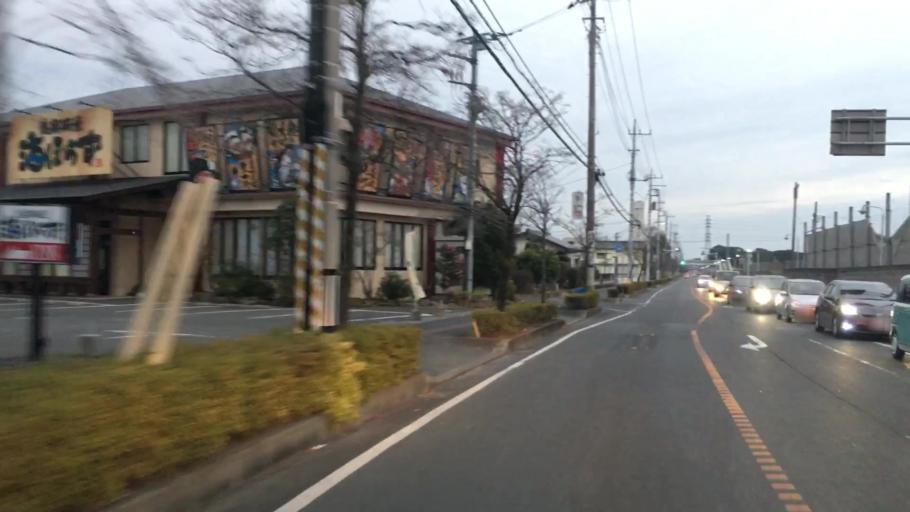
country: JP
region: Gunma
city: Ota
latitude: 36.3025
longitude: 139.3820
